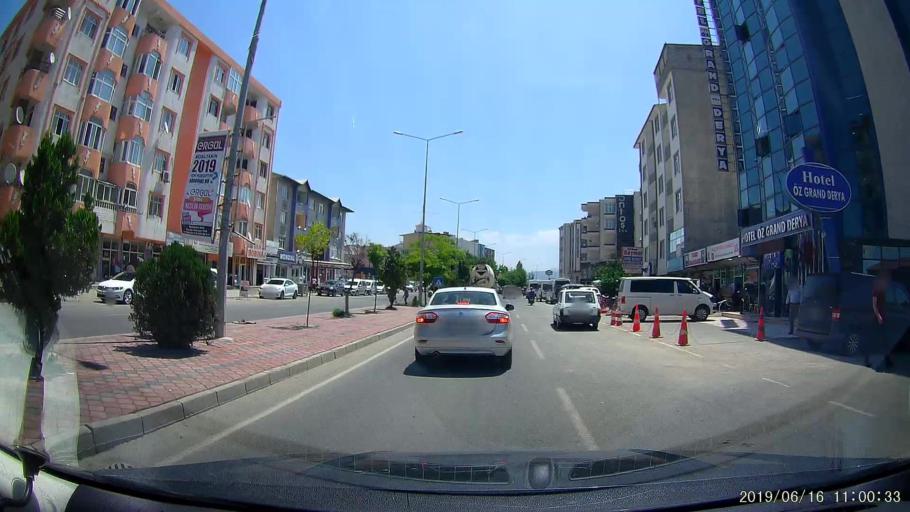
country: TR
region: Igdir
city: Igdir
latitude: 39.9182
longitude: 44.0446
